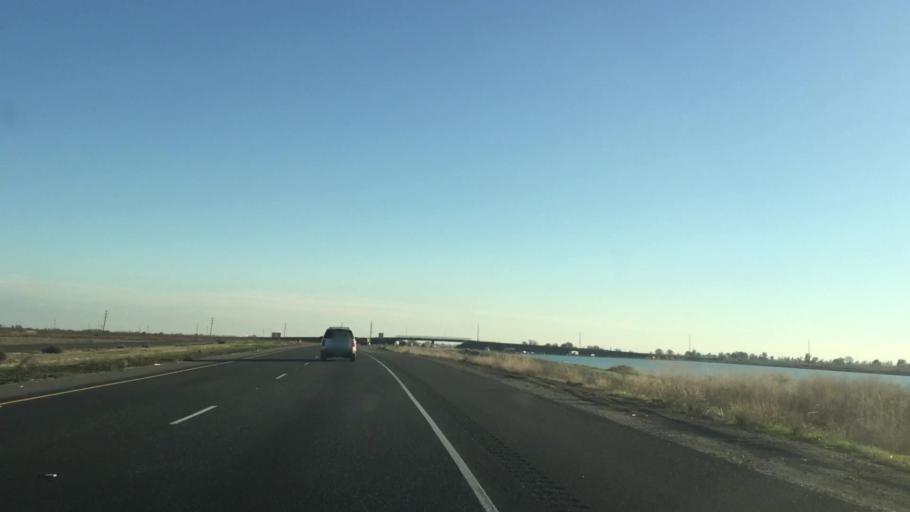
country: US
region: California
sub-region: Yuba County
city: Plumas Lake
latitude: 38.9030
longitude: -121.5479
